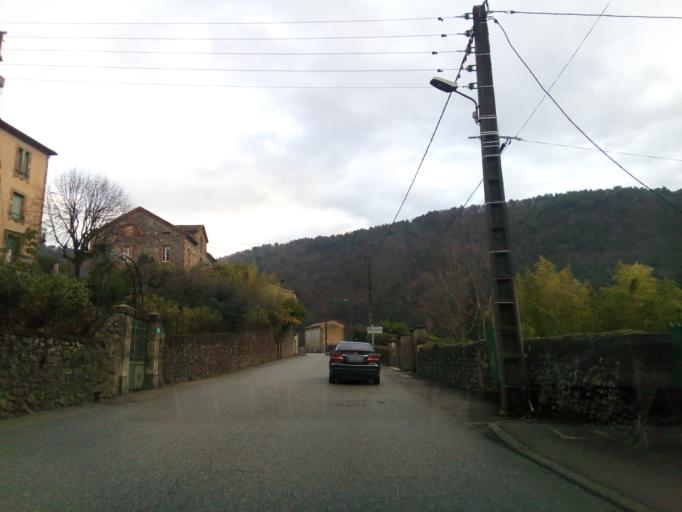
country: FR
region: Rhone-Alpes
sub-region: Departement de l'Ardeche
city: Saint-Sauveur-de-Montagut
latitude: 44.8046
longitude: 4.6195
